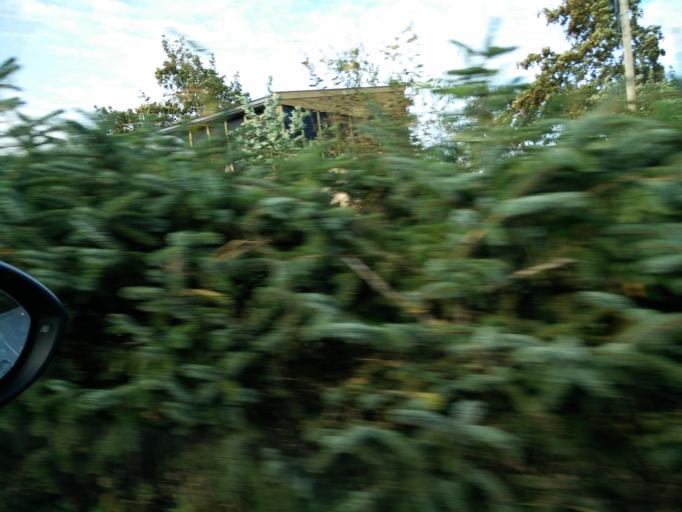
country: NO
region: Hordaland
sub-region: Sveio
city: Sveio
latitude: 59.5531
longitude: 5.3454
